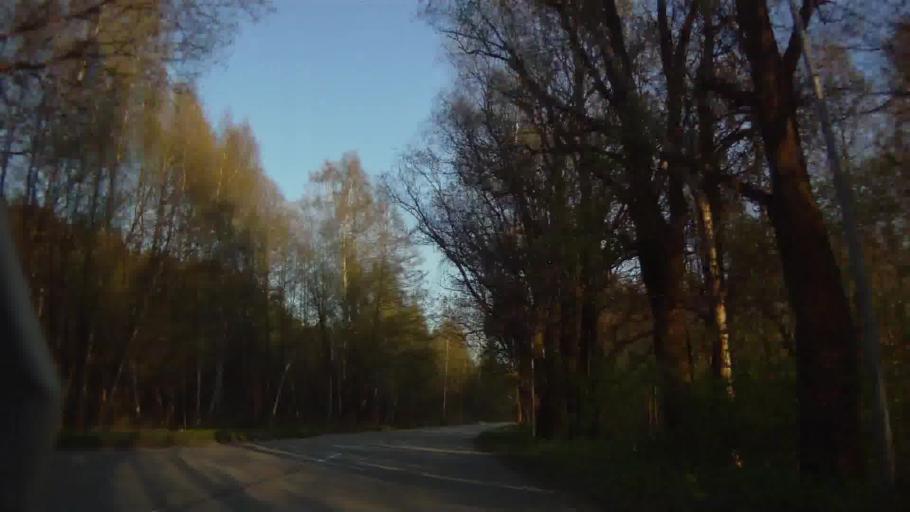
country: LV
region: Riga
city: Jaunciems
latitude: 57.0518
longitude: 24.1706
